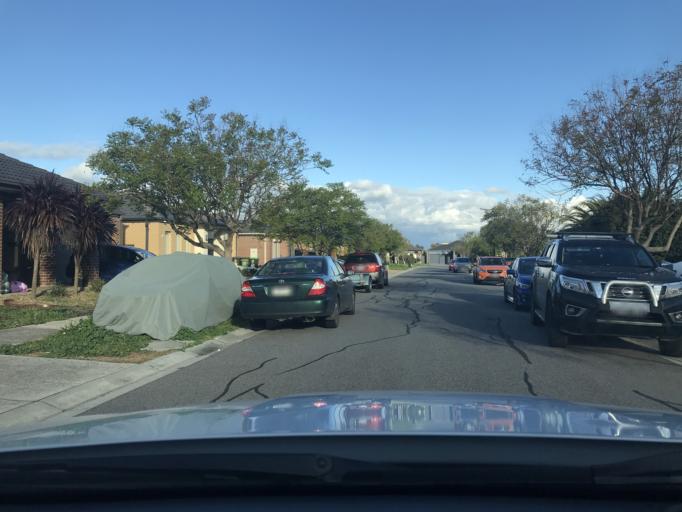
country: AU
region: Victoria
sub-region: Hume
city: Craigieburn
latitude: -37.5793
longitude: 144.9057
